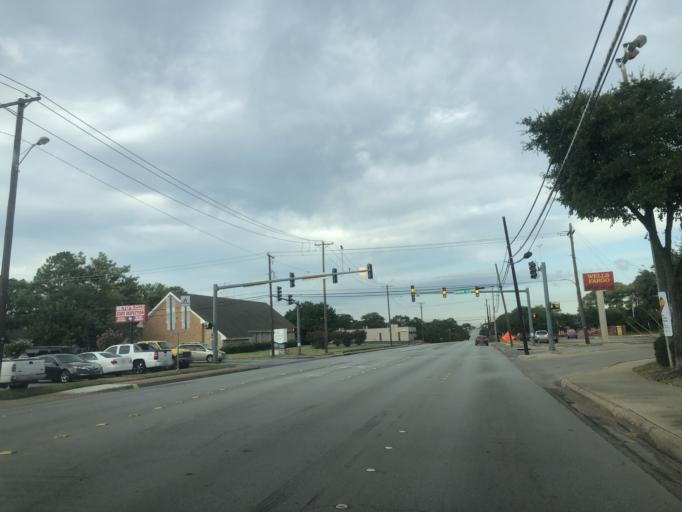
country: US
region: Texas
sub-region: Tarrant County
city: Hurst
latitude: 32.8236
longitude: -97.1638
